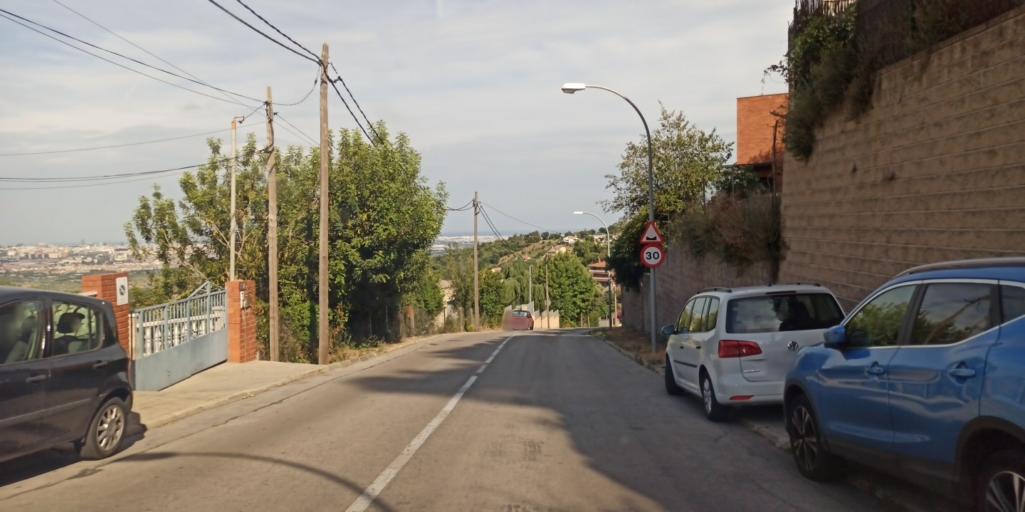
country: ES
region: Catalonia
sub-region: Provincia de Barcelona
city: Santa Coloma de Cervello
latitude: 41.3616
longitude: 2.0006
